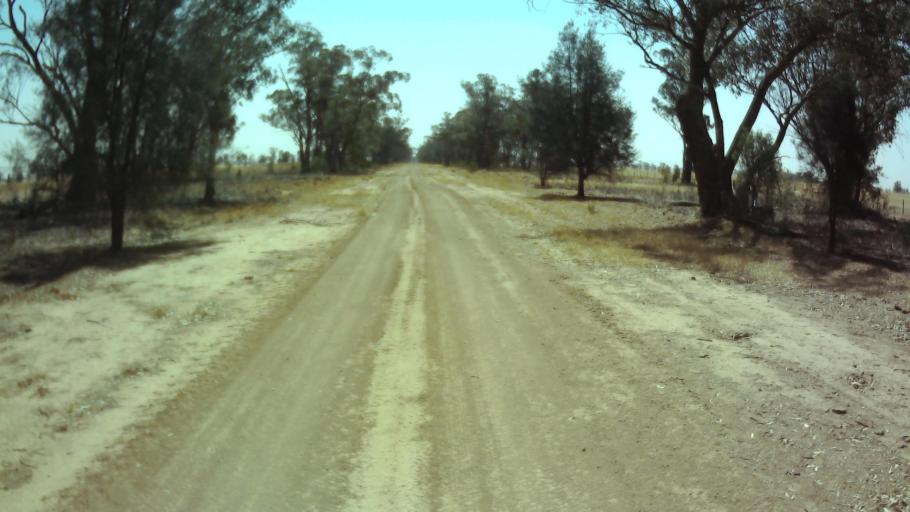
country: AU
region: New South Wales
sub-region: Weddin
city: Grenfell
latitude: -33.9326
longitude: 147.8009
